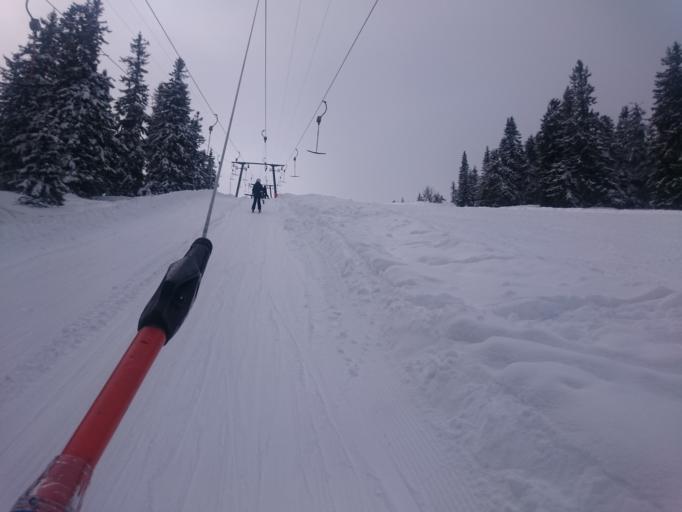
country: SE
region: Dalarna
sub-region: Malung-Saelens kommun
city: Malung
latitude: 61.1623
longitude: 13.1675
